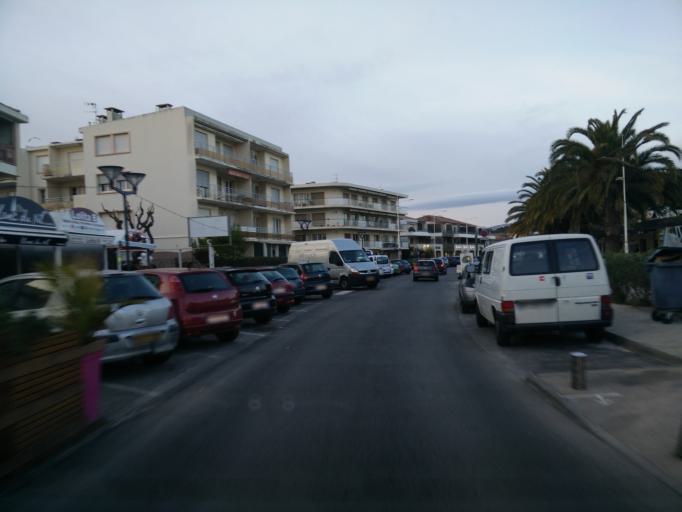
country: FR
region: Provence-Alpes-Cote d'Azur
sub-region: Departement du Var
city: La Seyne-sur-Mer
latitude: 43.0797
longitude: 5.8943
